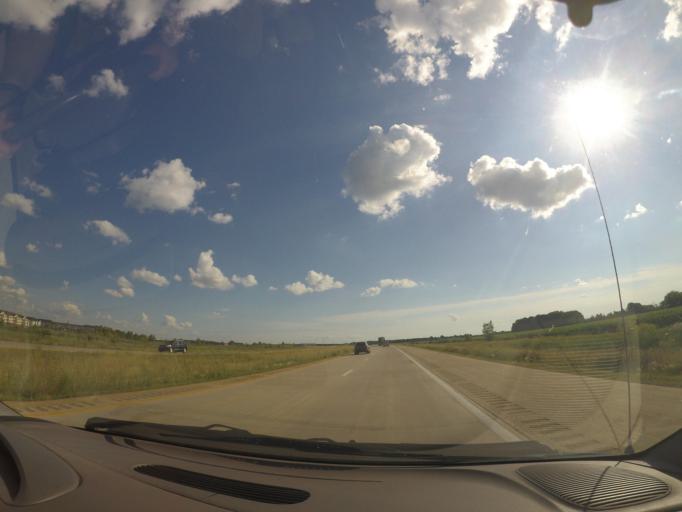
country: US
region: Ohio
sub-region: Lucas County
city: Waterville
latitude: 41.5169
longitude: -83.7482
